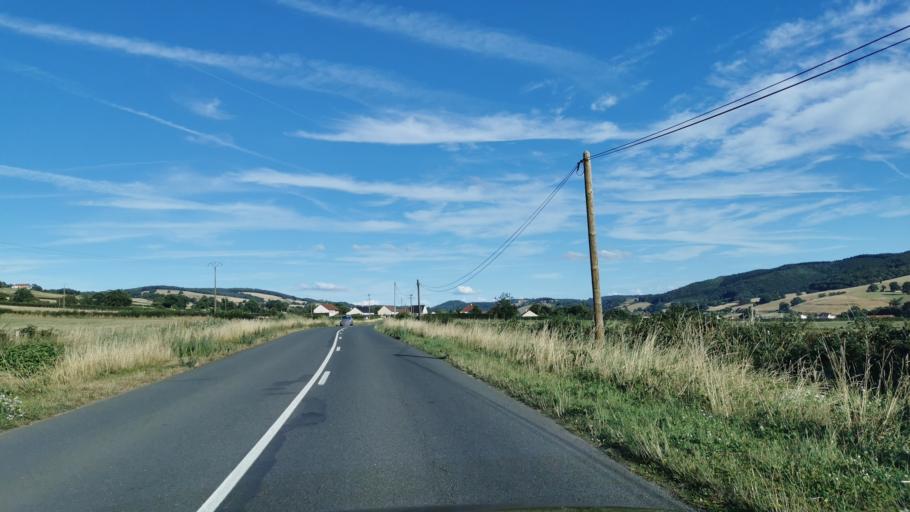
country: FR
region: Bourgogne
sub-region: Departement de Saone-et-Loire
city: Marmagne
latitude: 46.8508
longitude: 4.3297
